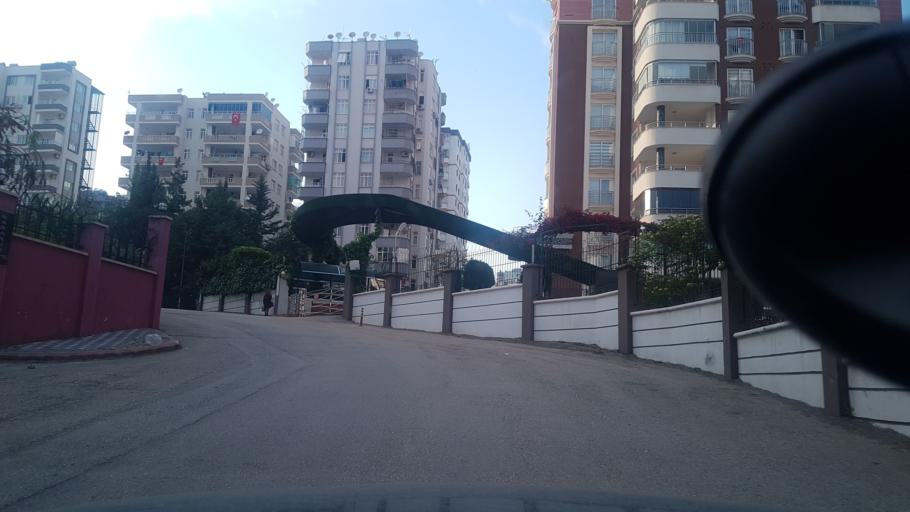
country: TR
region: Adana
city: Seyhan
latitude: 37.0465
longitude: 35.2762
